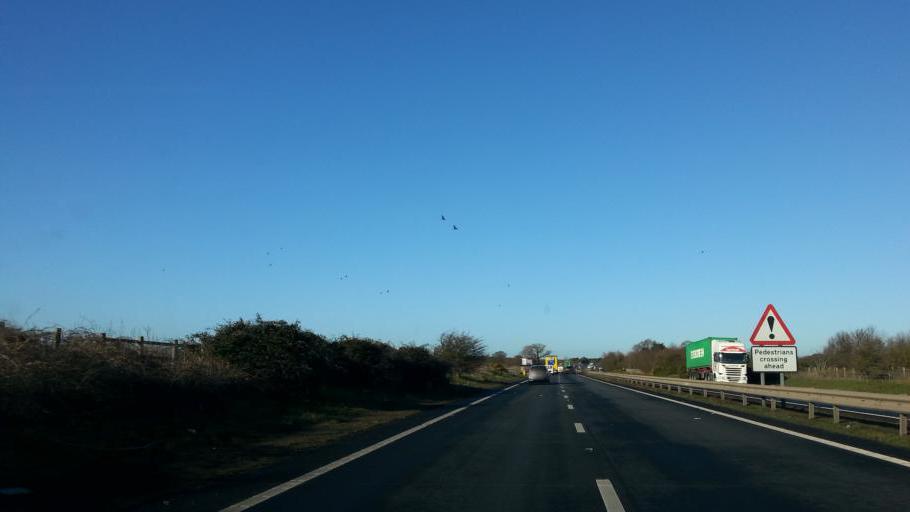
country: GB
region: England
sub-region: Suffolk
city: Kesgrave
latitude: 52.0174
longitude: 1.2697
